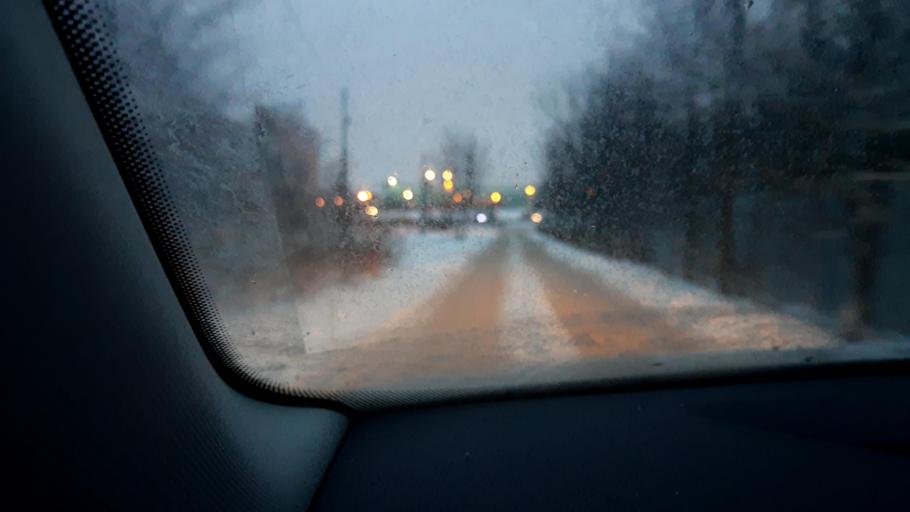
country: RU
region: Moskovskaya
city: Yam
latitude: 55.4810
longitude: 37.7168
